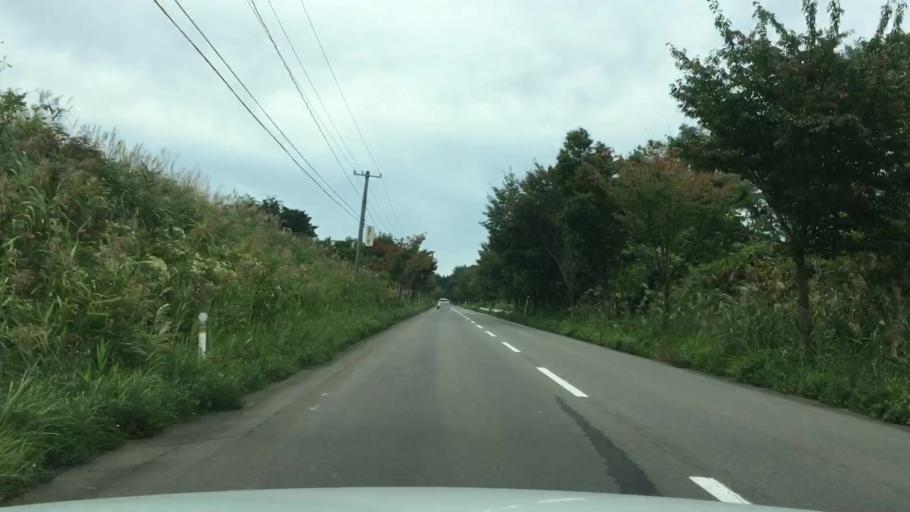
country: JP
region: Aomori
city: Shimokizukuri
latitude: 40.7126
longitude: 140.2871
